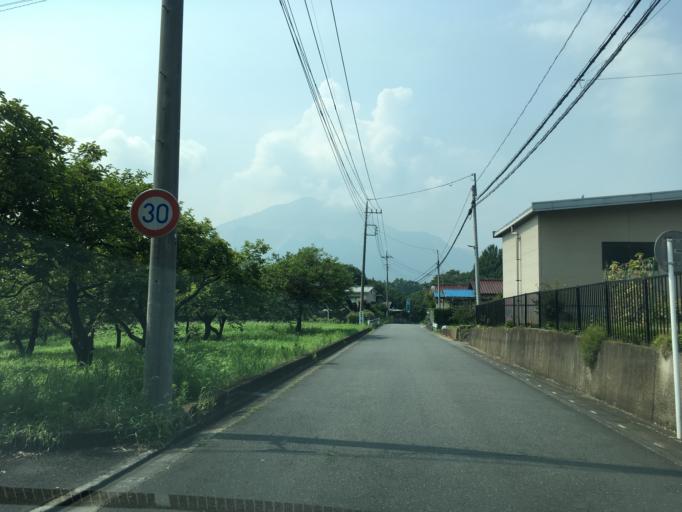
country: JP
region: Saitama
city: Chichibu
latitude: 36.0041
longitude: 139.1037
